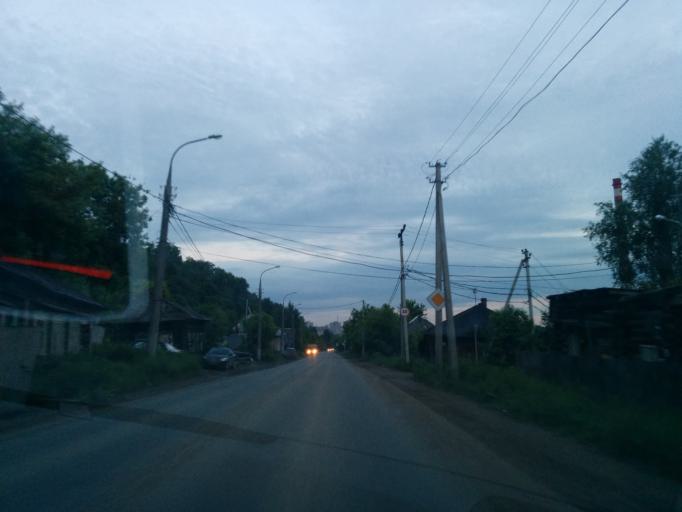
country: RU
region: Perm
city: Perm
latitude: 58.0470
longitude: 56.3231
